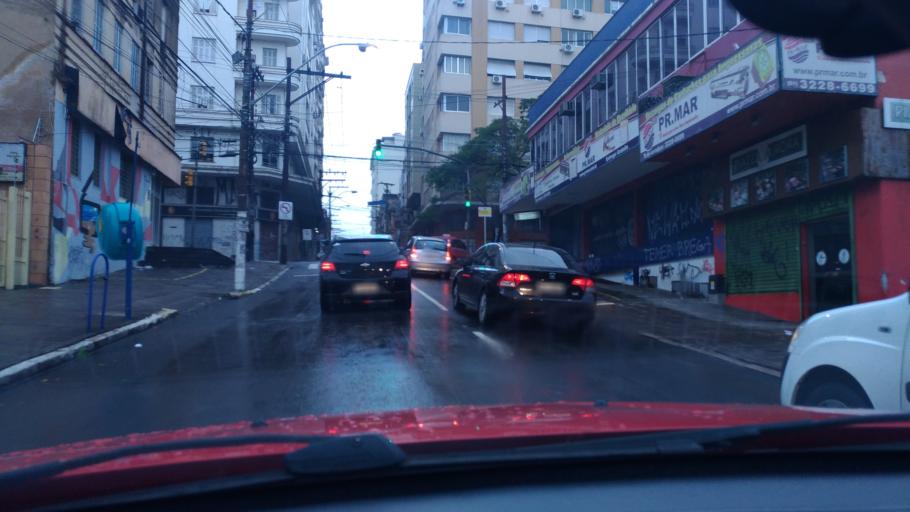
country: BR
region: Rio Grande do Sul
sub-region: Porto Alegre
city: Porto Alegre
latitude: -30.0274
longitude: -51.2173
